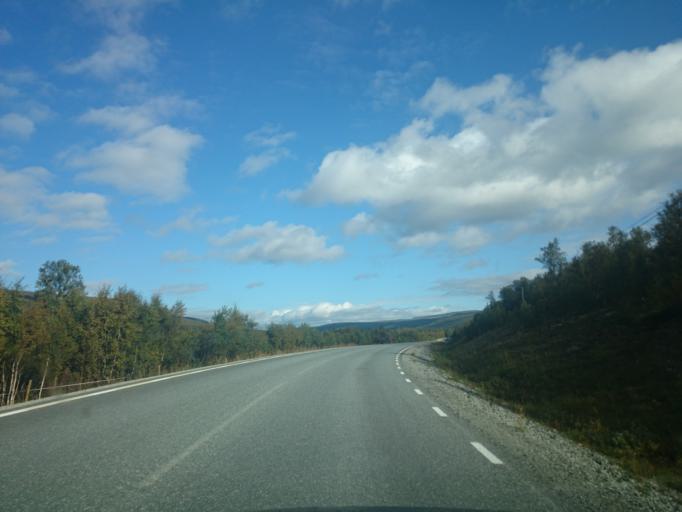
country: NO
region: Sor-Trondelag
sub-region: Tydal
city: Aas
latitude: 62.6487
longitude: 12.4251
